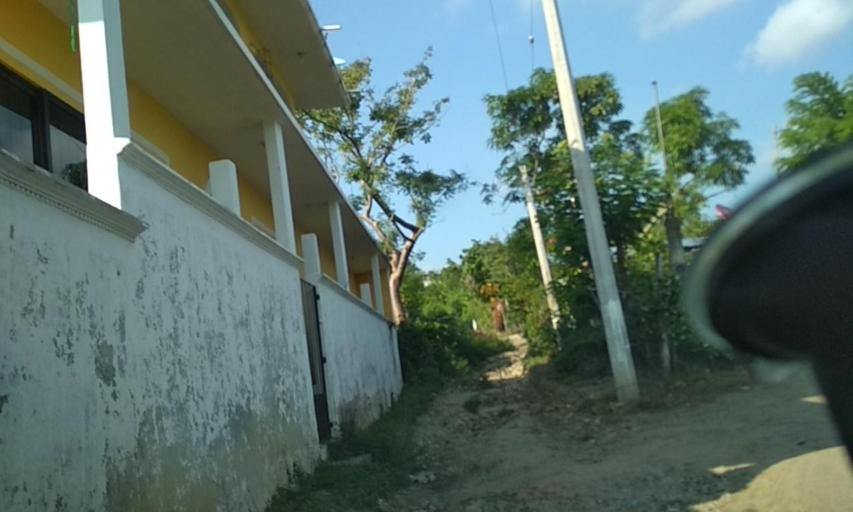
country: MX
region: Veracruz
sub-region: Papantla
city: Polutla
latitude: 20.5999
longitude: -97.2587
